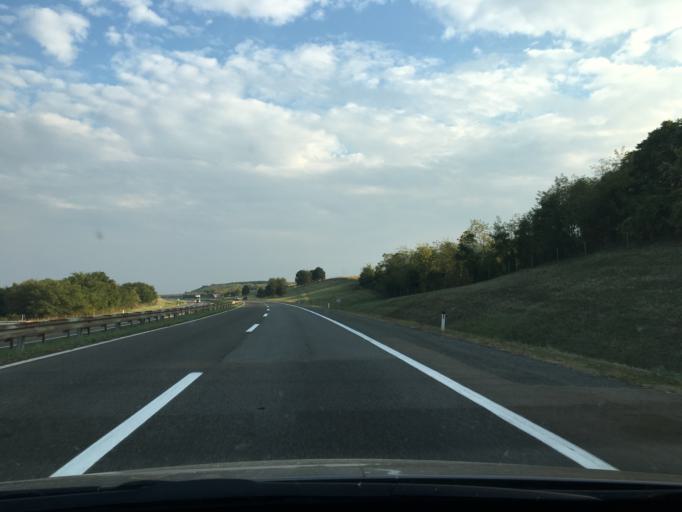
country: RS
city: Lugavcina
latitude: 44.4901
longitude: 21.0235
